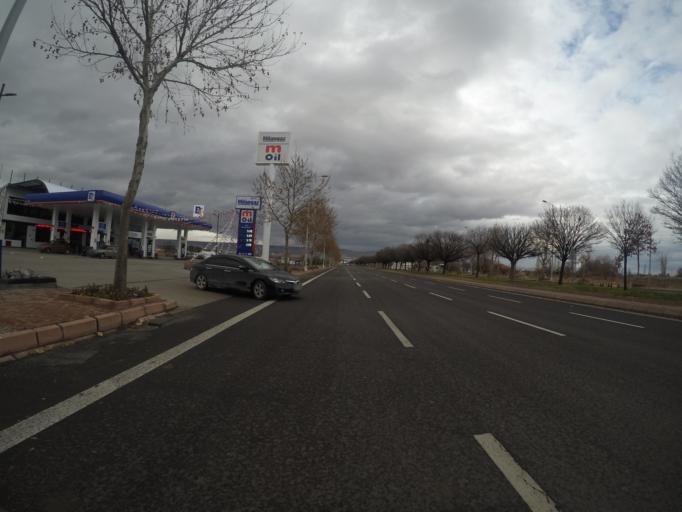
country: TR
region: Kayseri
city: Kayseri
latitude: 38.7589
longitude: 35.4824
